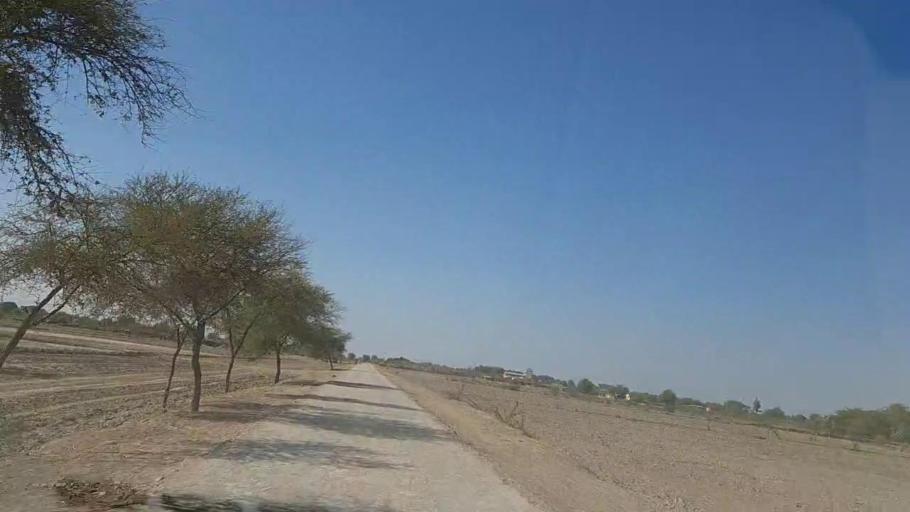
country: PK
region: Sindh
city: Digri
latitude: 25.1216
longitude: 69.0771
